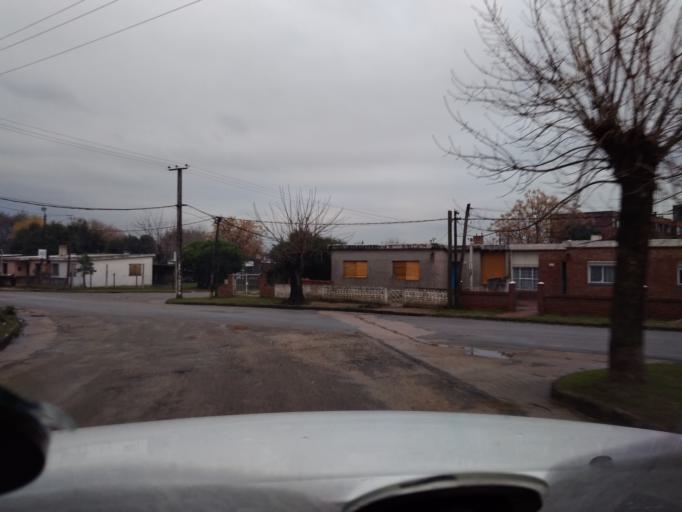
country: UY
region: Florida
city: Florida
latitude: -34.1075
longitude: -56.2135
